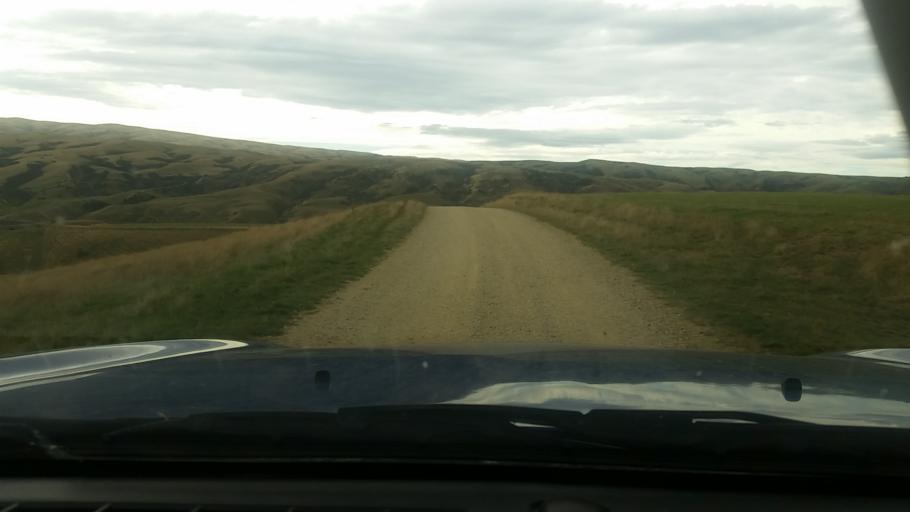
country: NZ
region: Otago
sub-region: Clutha District
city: Balclutha
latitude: -45.7171
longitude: 169.5313
